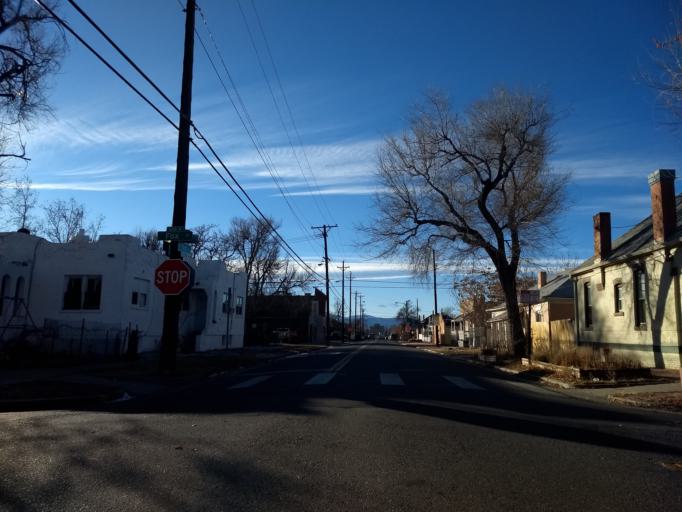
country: US
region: Colorado
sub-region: Denver County
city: Denver
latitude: 39.7210
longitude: -104.9952
